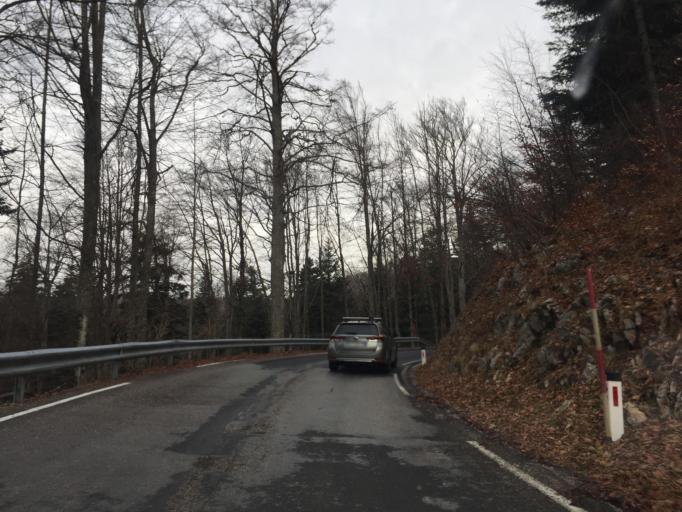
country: SI
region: Nova Gorica
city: Sempas
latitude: 46.0065
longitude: 13.7821
